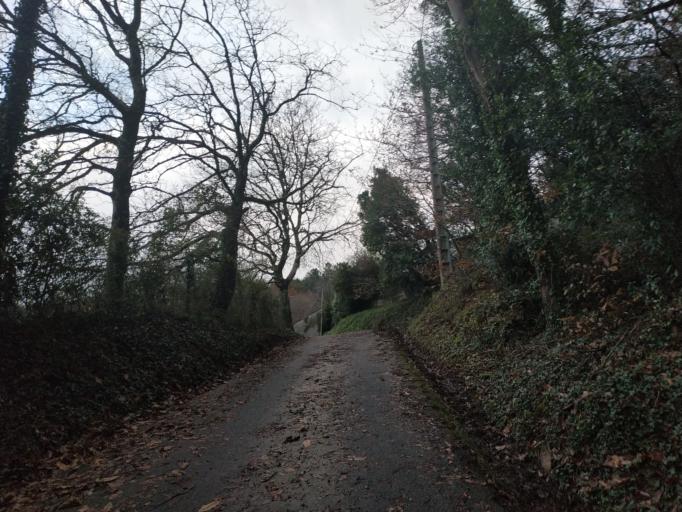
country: ES
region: Galicia
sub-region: Provincia de Pontevedra
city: Silleda
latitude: 42.7825
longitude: -8.1642
